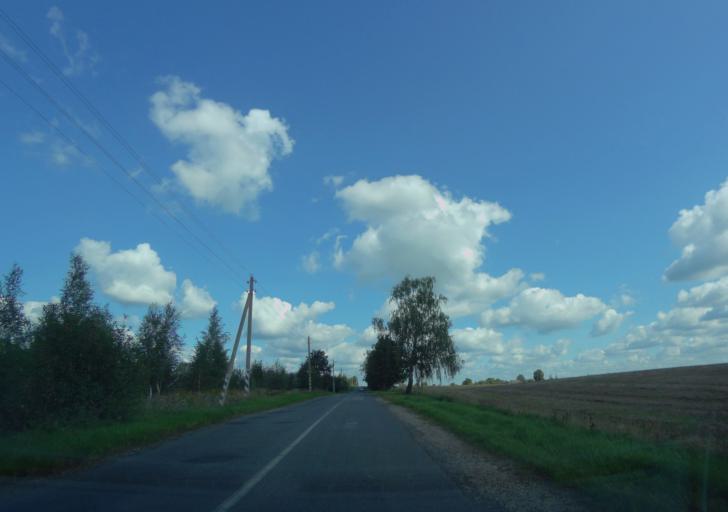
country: BY
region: Minsk
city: Zyembin
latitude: 54.4060
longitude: 28.4022
